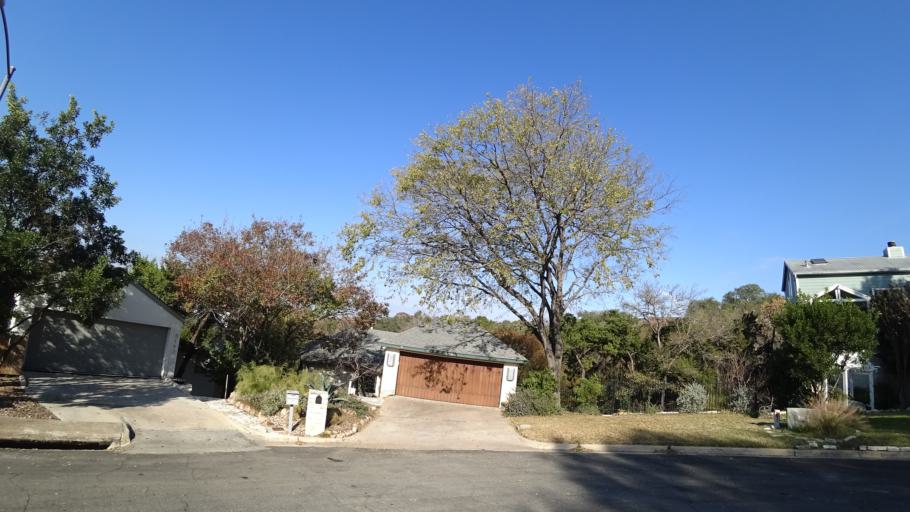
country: US
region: Texas
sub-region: Williamson County
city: Jollyville
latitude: 30.3913
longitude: -97.7607
